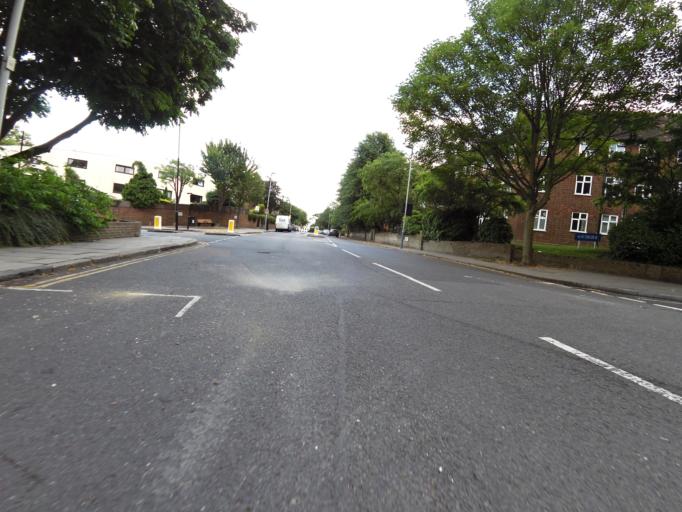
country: GB
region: England
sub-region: Greater London
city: Holloway
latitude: 51.5543
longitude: -0.1287
